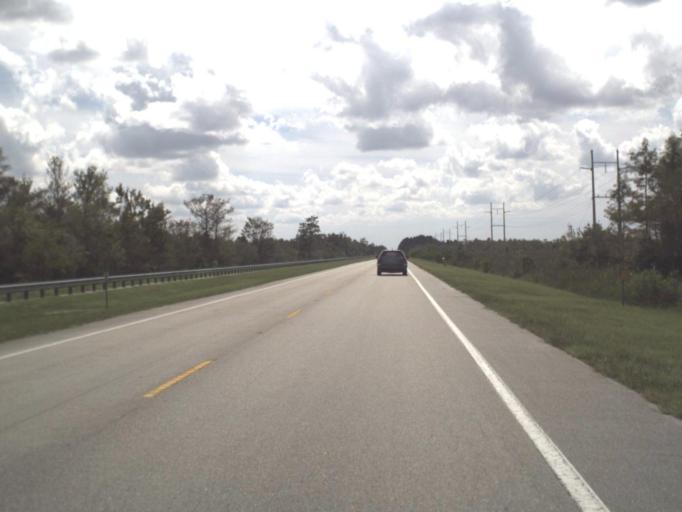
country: US
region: Florida
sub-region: Collier County
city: Lely Resort
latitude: 26.0169
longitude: -81.3458
